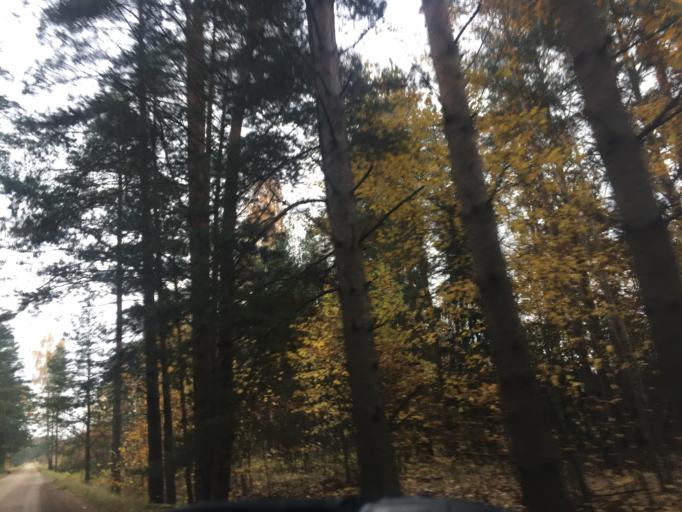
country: LV
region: Jaunpils
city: Jaunpils
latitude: 56.6887
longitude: 23.1166
